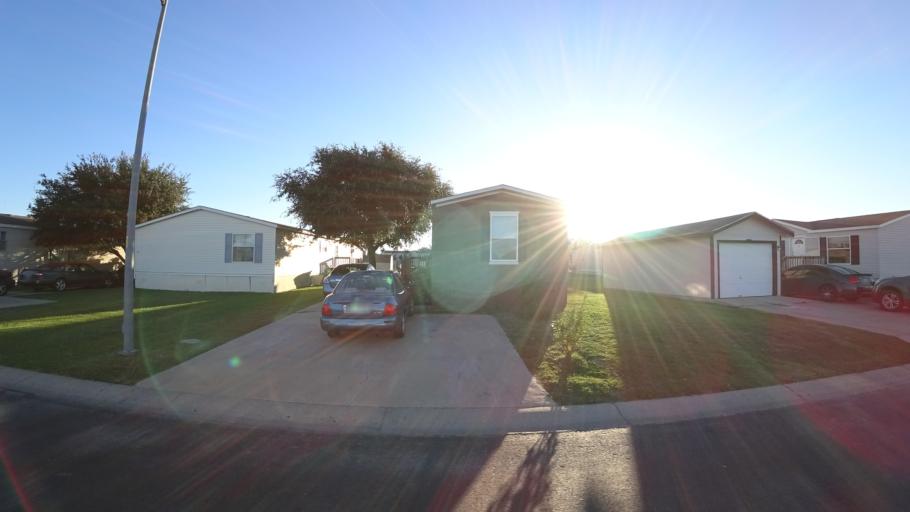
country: US
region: Texas
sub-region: Travis County
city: Manor
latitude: 30.3154
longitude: -97.6264
